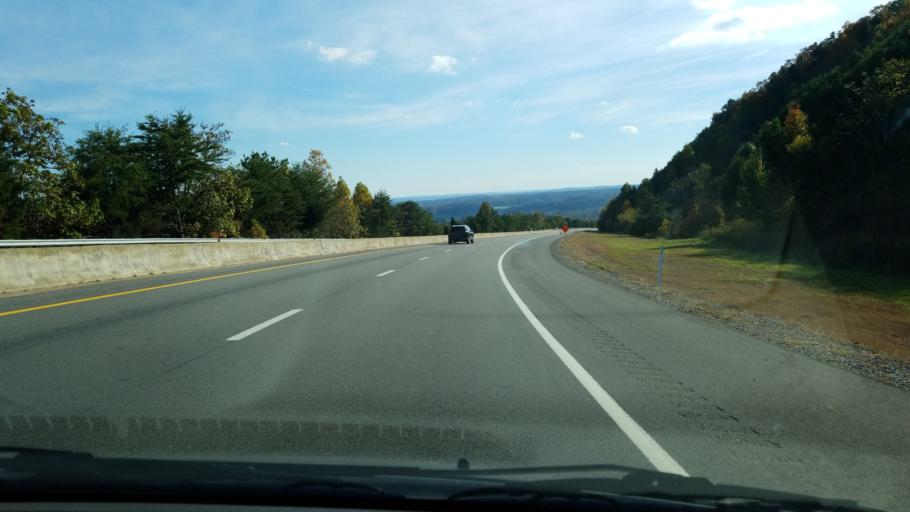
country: US
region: Tennessee
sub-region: Hamilton County
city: Sale Creek
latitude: 35.3238
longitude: -85.1606
